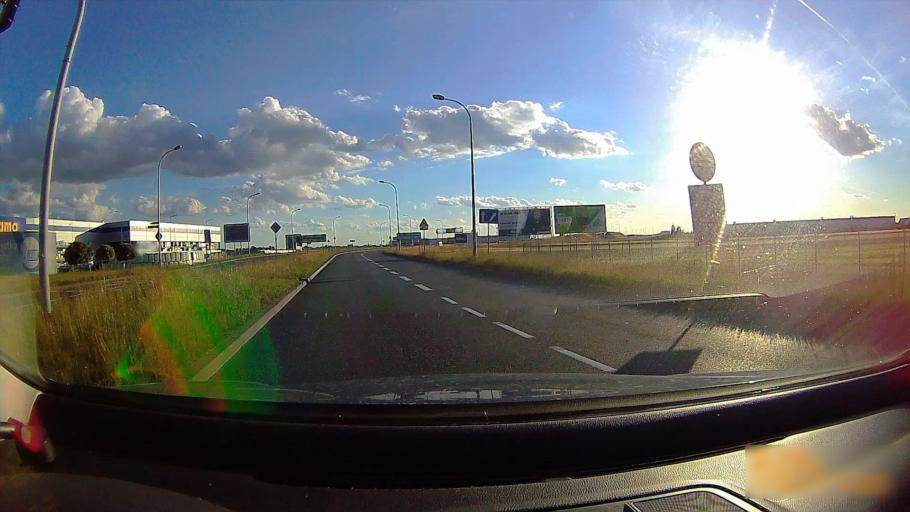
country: PL
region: Greater Poland Voivodeship
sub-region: Kalisz
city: Kalisz
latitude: 51.7394
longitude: 18.0429
